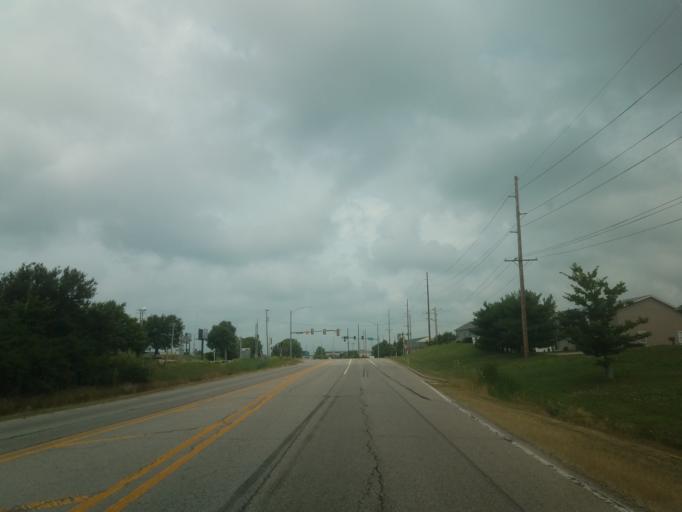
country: US
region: Illinois
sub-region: McLean County
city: Bloomington
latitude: 40.4940
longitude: -89.0194
